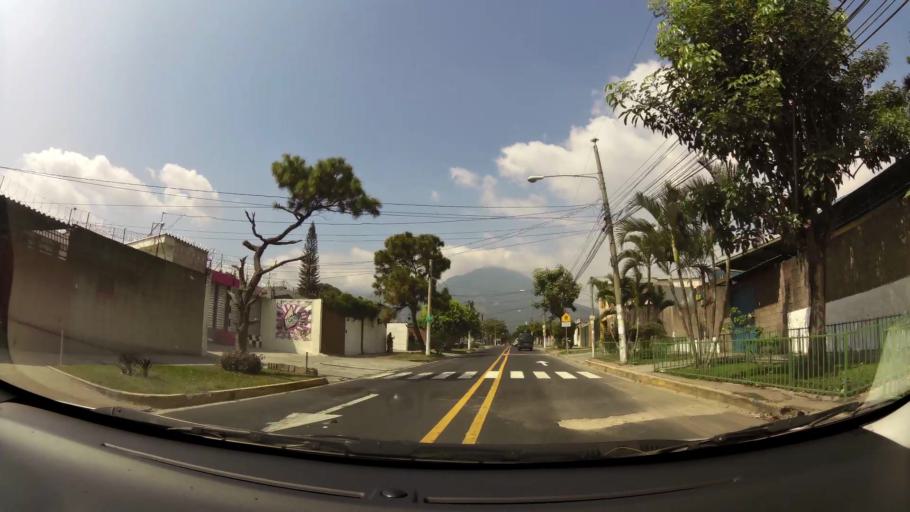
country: SV
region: San Salvador
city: Mejicanos
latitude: 13.7116
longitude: -89.2162
